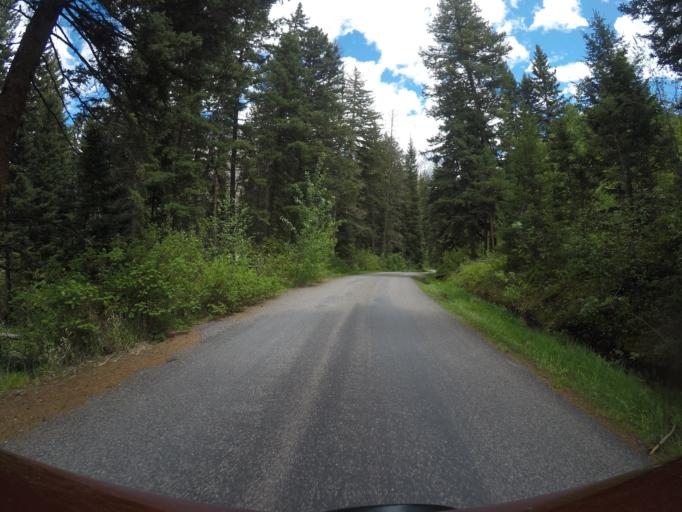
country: US
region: Montana
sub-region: Park County
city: Livingston
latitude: 45.4984
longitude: -110.5259
